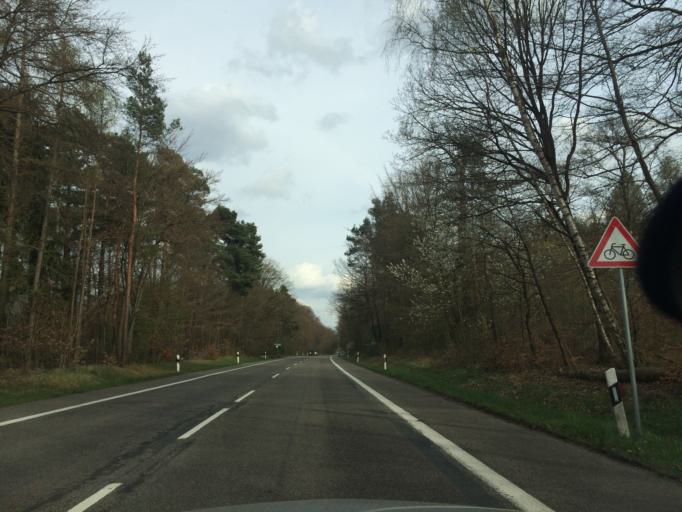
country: DE
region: Hesse
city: Niederrad
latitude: 50.0293
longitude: 8.6281
